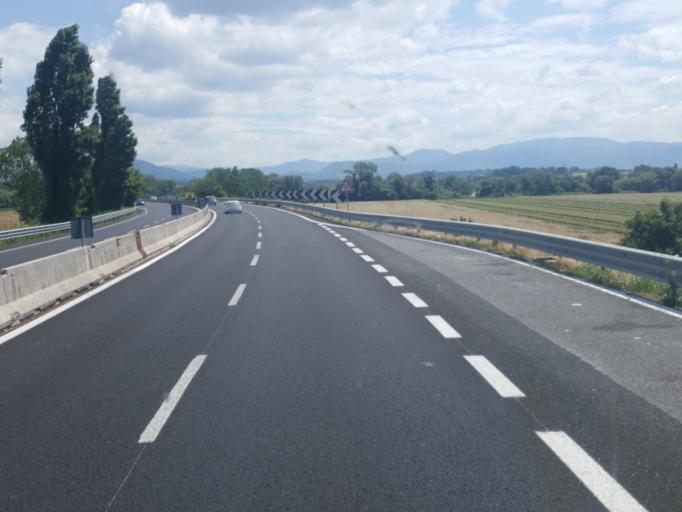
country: IT
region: Latium
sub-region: Citta metropolitana di Roma Capitale
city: Fiano Romano
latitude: 42.1499
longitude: 12.6302
